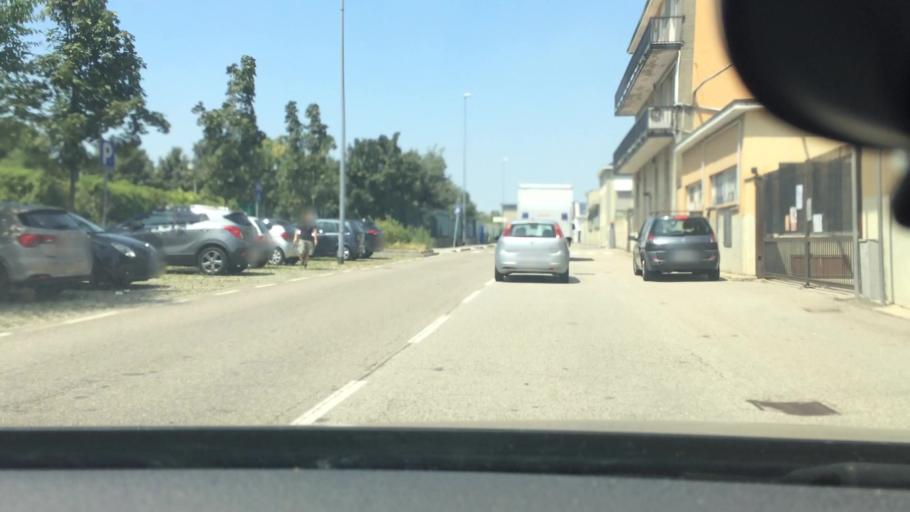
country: IT
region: Lombardy
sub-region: Citta metropolitana di Milano
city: Pero
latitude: 45.5029
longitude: 9.0879
